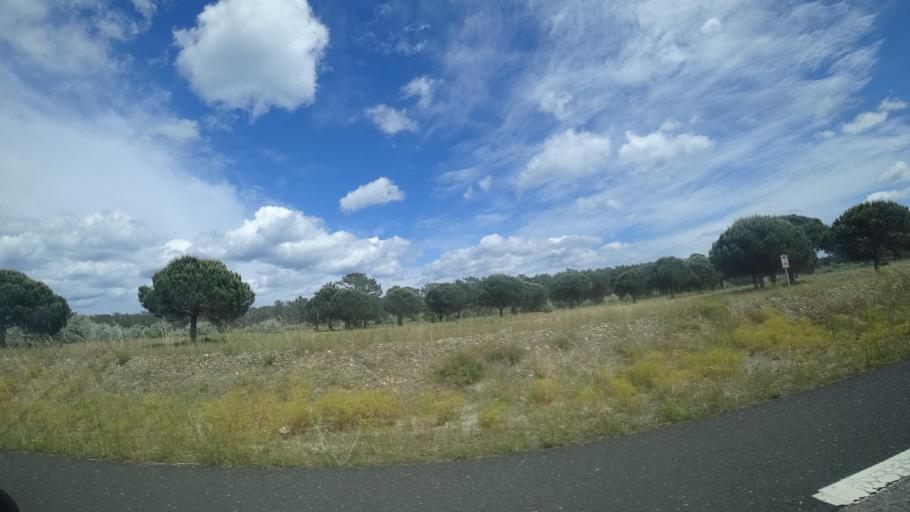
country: FR
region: Languedoc-Roussillon
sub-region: Departement des Pyrenees-Orientales
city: Le Barcares
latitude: 42.8170
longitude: 3.0306
